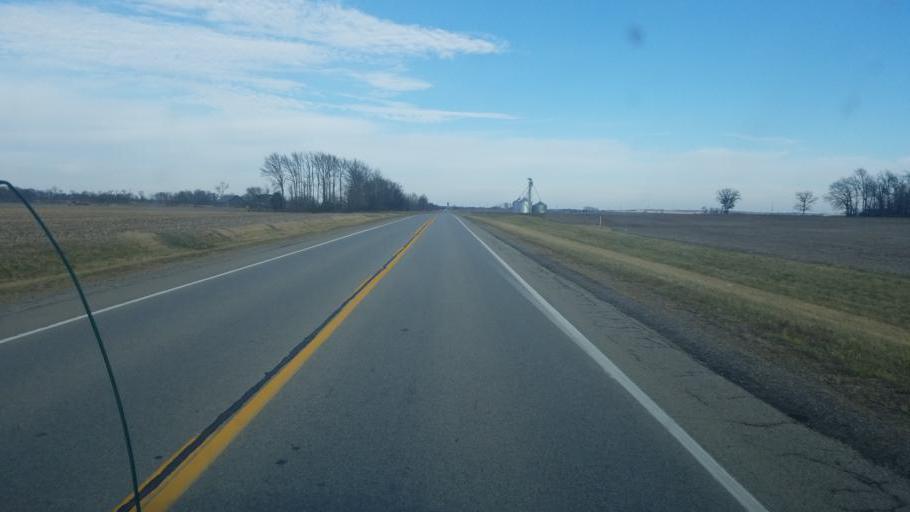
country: US
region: Illinois
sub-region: White County
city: Carmi
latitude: 38.1364
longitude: -88.0933
